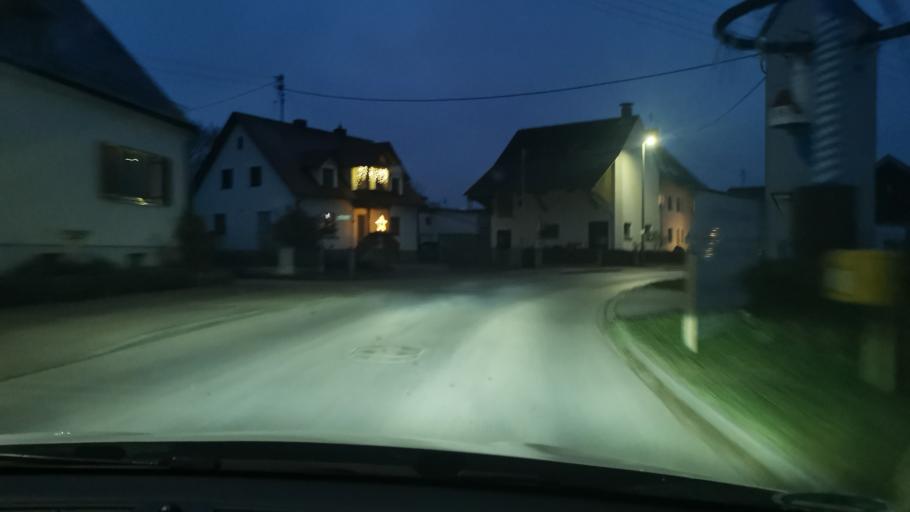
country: DE
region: Bavaria
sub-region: Swabia
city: Petersdorf
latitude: 48.5564
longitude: 11.0096
